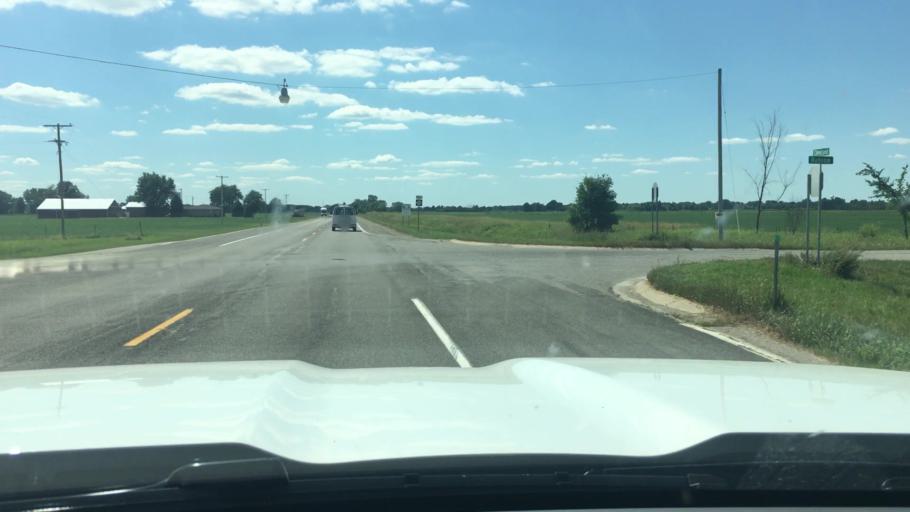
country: US
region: Michigan
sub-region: Clinton County
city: Ovid
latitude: 43.1760
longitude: -84.4475
